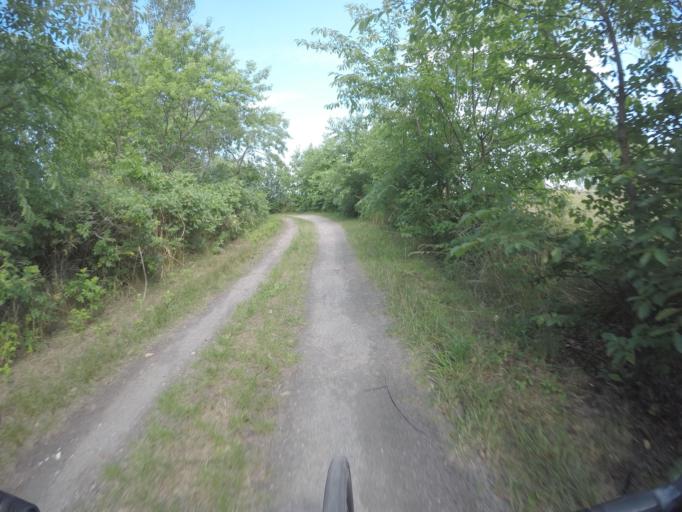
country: DE
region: Mecklenburg-Vorpommern
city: Altefahr
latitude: 54.3657
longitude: 13.1244
